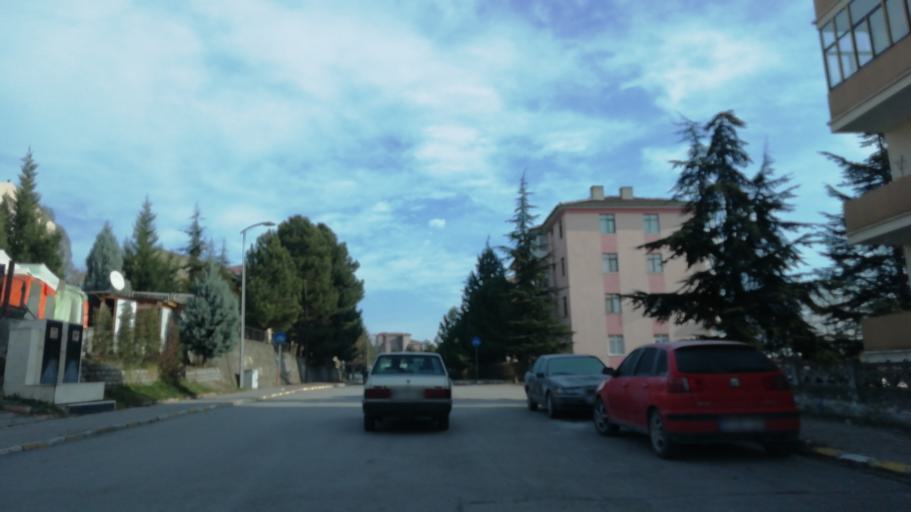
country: TR
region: Karabuk
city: Safranbolu
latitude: 41.2528
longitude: 32.6736
